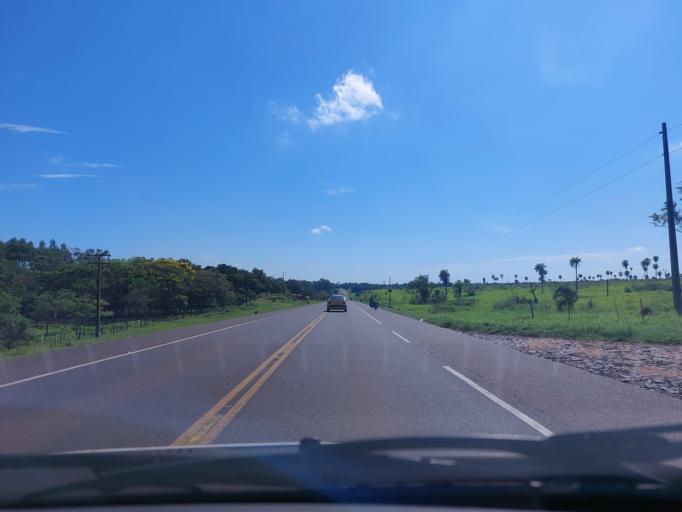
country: PY
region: San Pedro
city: Guayaybi
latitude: -24.6510
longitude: -56.4669
